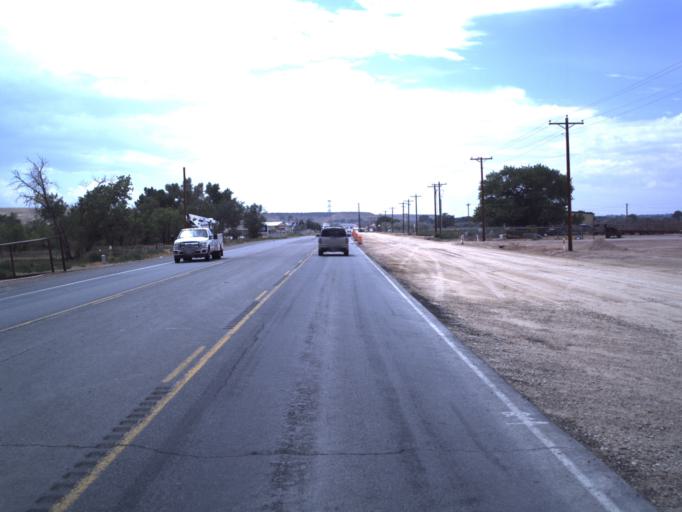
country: US
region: Utah
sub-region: Duchesne County
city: Roosevelt
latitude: 40.2700
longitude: -110.0369
